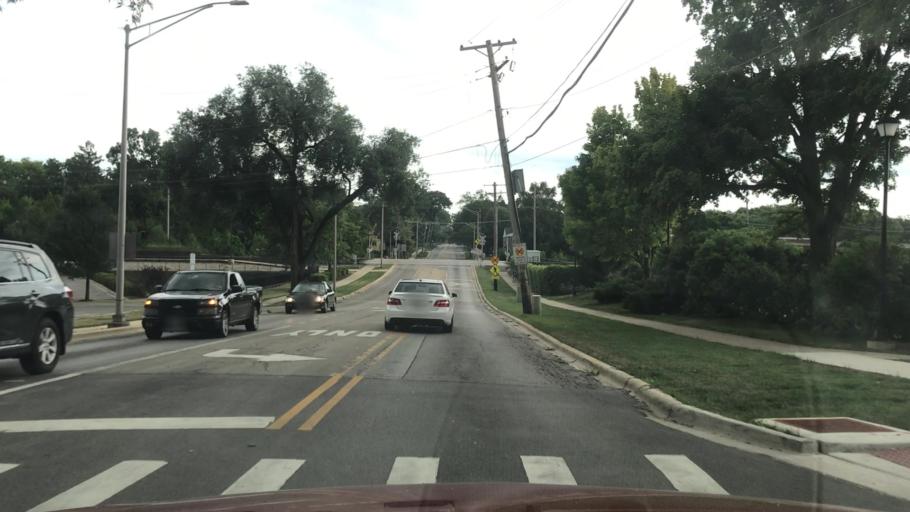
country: US
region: Illinois
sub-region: DuPage County
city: Wheaton
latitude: 41.8688
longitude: -88.0920
